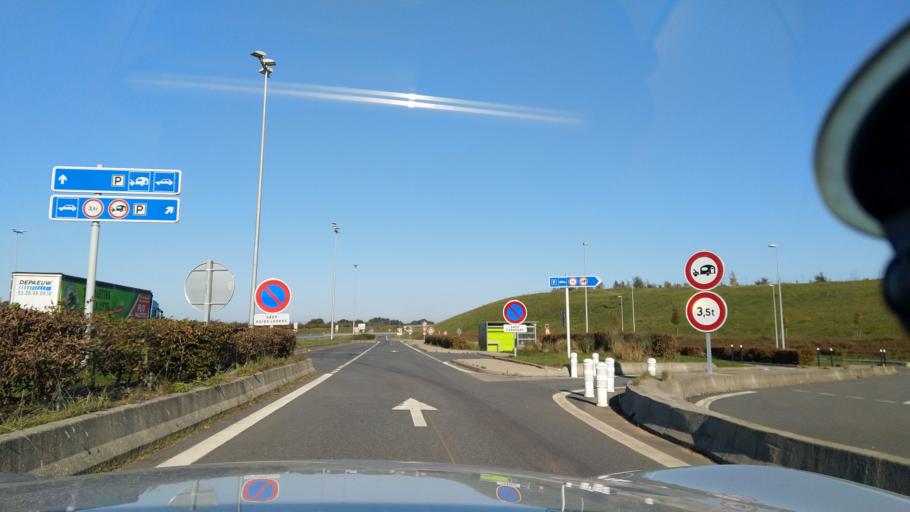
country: FR
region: Haute-Normandie
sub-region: Departement de la Seine-Maritime
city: Villers-Ecalles
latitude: 49.5490
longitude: 0.9213
